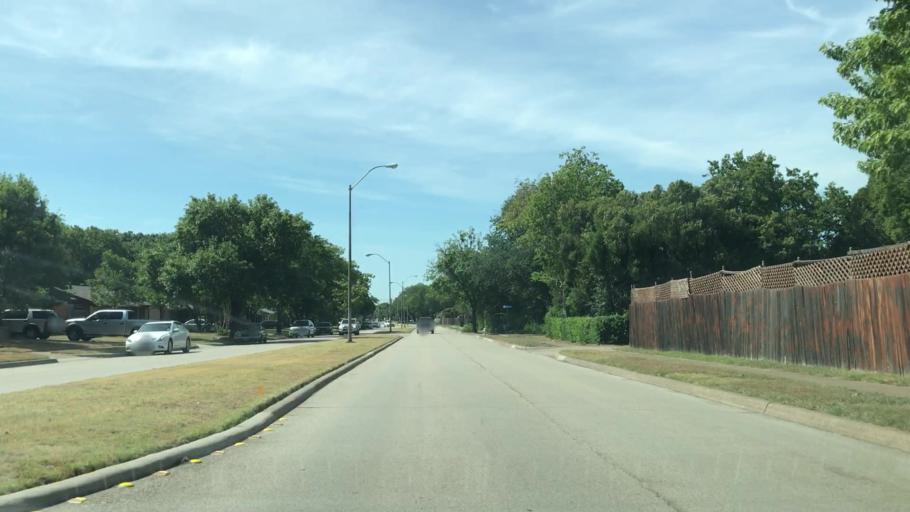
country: US
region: Texas
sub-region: Dallas County
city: Richardson
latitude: 32.9521
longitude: -96.7142
